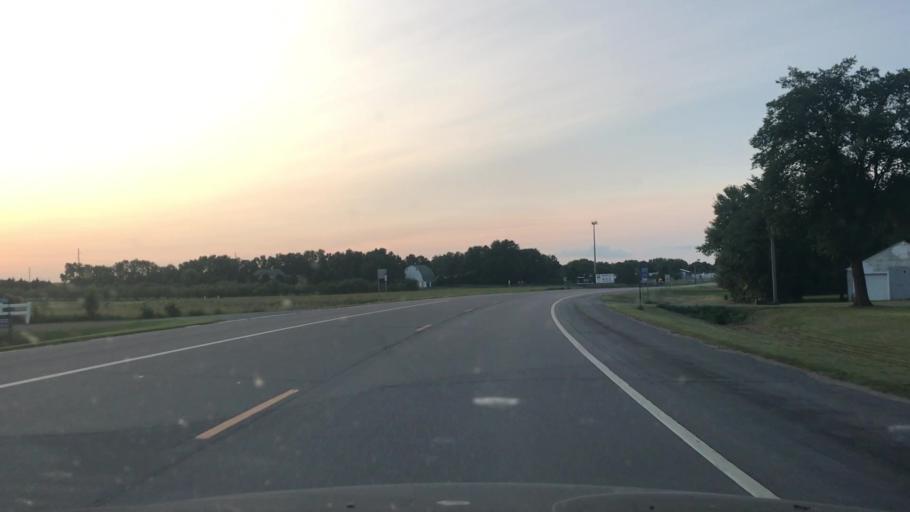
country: US
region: Minnesota
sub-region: Redwood County
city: Redwood Falls
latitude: 44.5256
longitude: -95.1191
